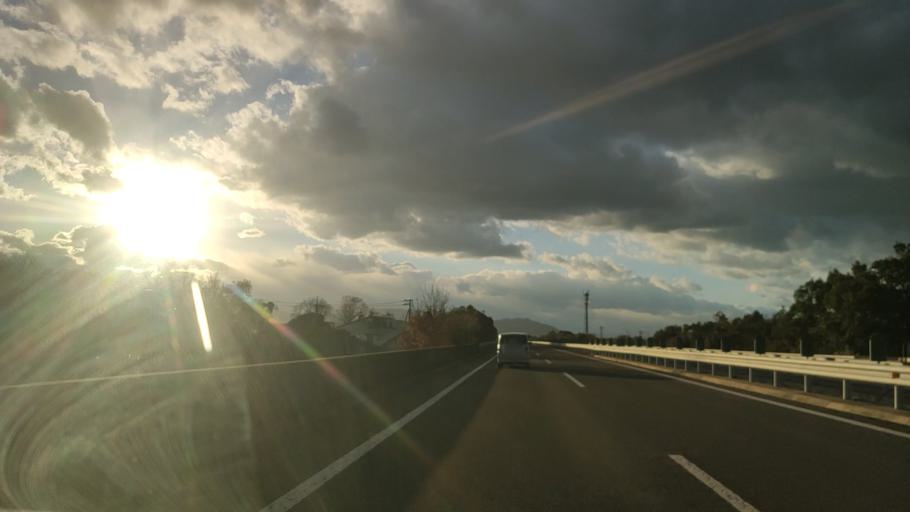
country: JP
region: Ehime
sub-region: Shikoku-chuo Shi
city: Matsuyama
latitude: 33.7856
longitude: 132.8589
